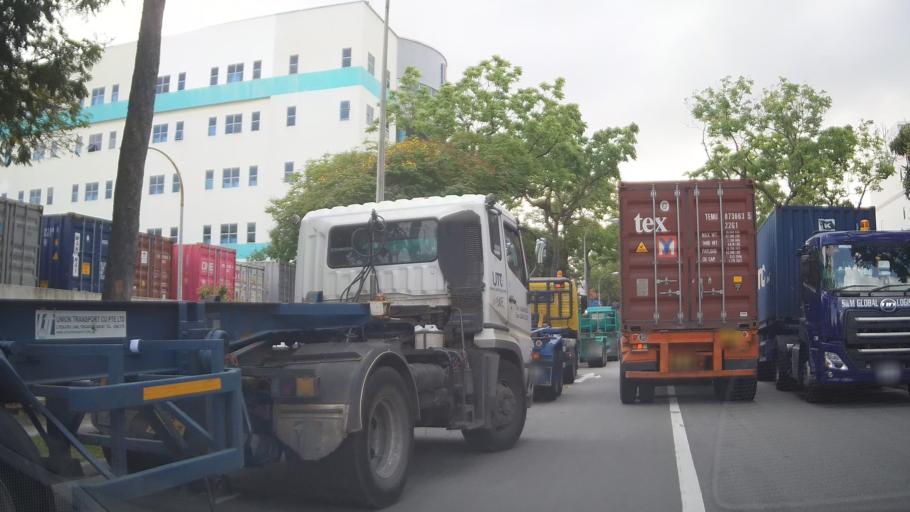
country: MY
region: Johor
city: Johor Bahru
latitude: 1.3208
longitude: 103.6421
